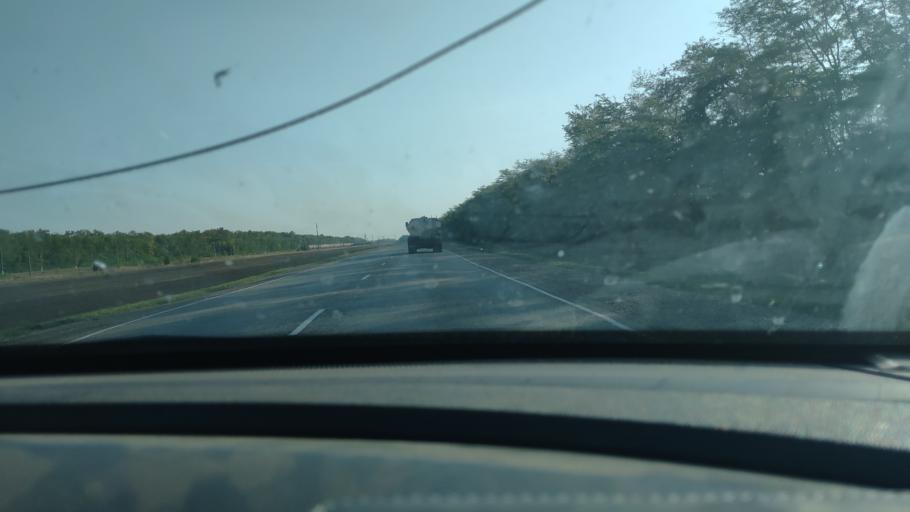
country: RU
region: Krasnodarskiy
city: Starominskaya
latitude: 46.4846
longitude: 39.0542
